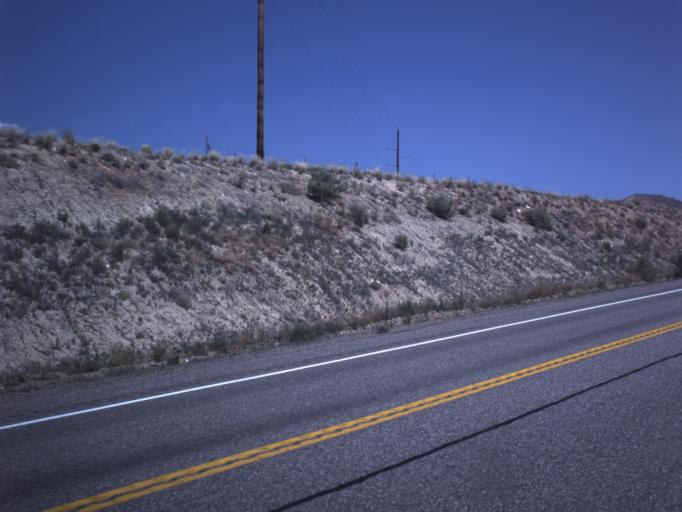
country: US
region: Utah
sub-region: Emery County
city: Ferron
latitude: 38.8927
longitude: -111.2799
